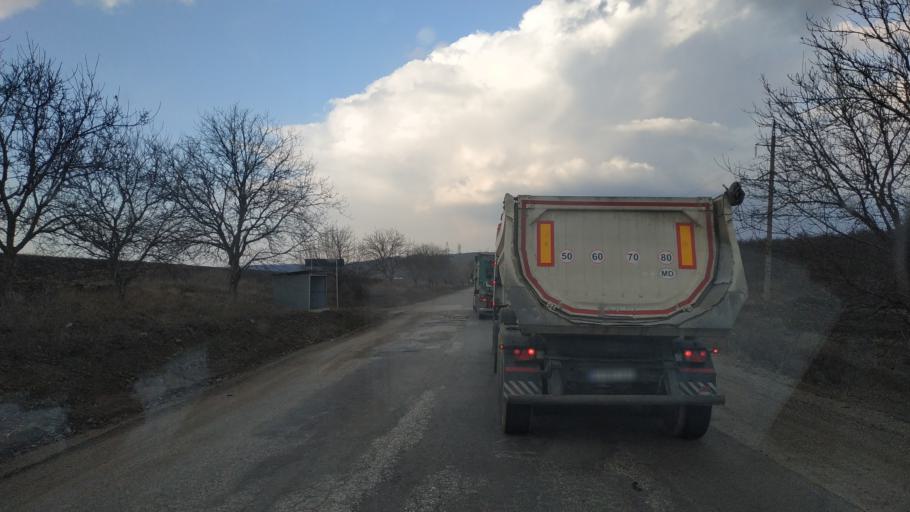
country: MD
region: Anenii Noi
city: Anenii Noi
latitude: 46.9804
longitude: 29.2843
